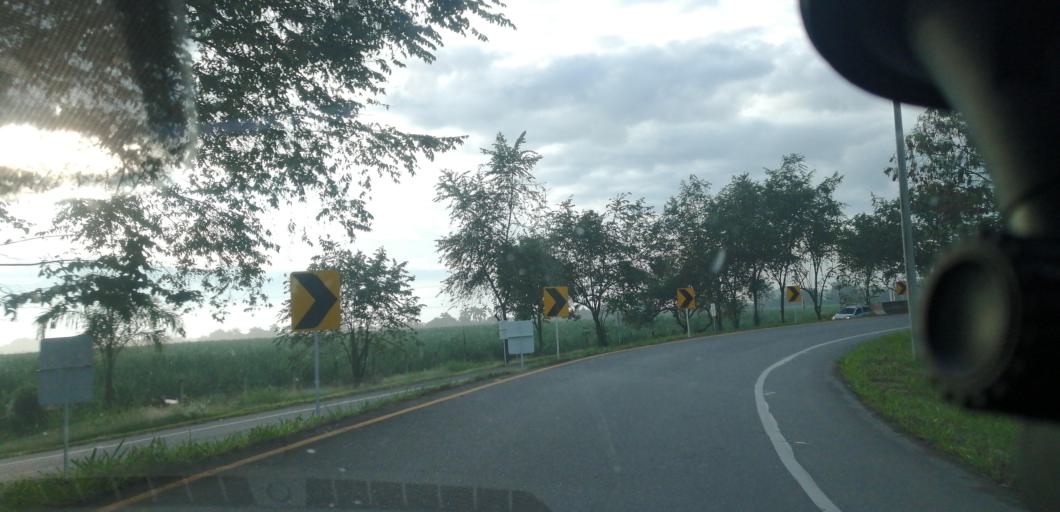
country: CO
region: Valle del Cauca
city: Palmira
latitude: 3.5243
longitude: -76.3364
